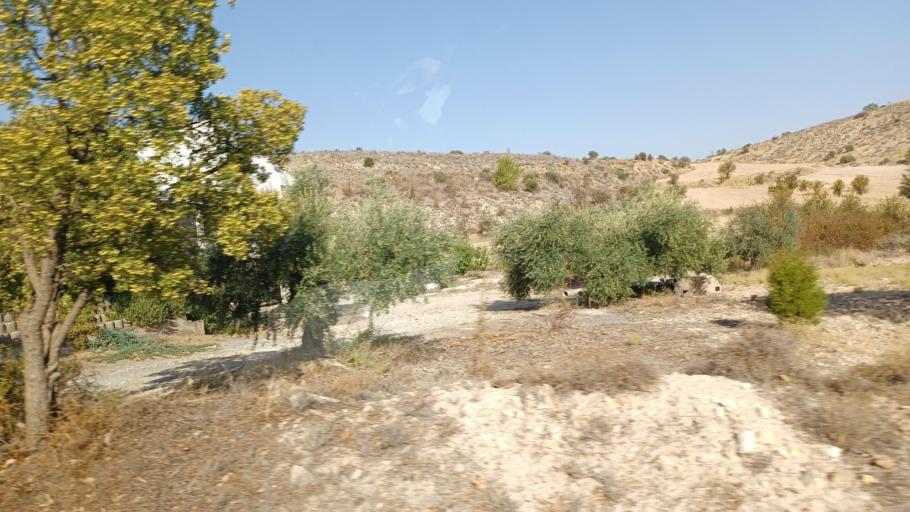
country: CY
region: Lefkosia
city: Alampra
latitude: 34.9845
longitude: 33.3575
